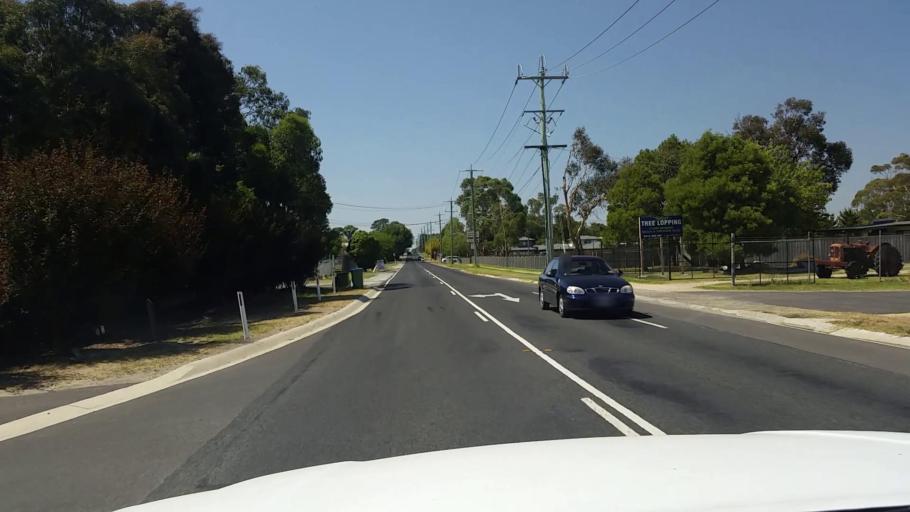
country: AU
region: Victoria
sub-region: Mornington Peninsula
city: Tyabb
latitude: -38.2613
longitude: 145.1804
